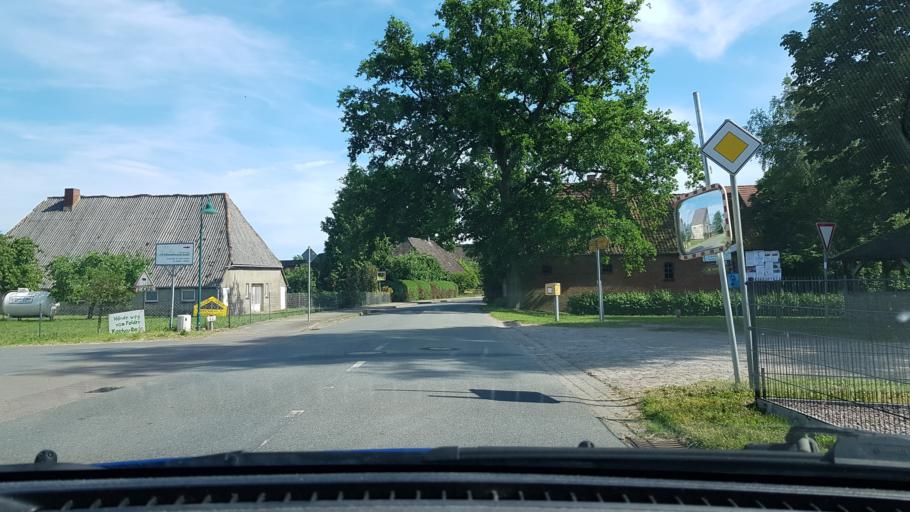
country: DE
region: Lower Saxony
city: Neu Darchau
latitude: 53.3236
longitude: 10.9083
